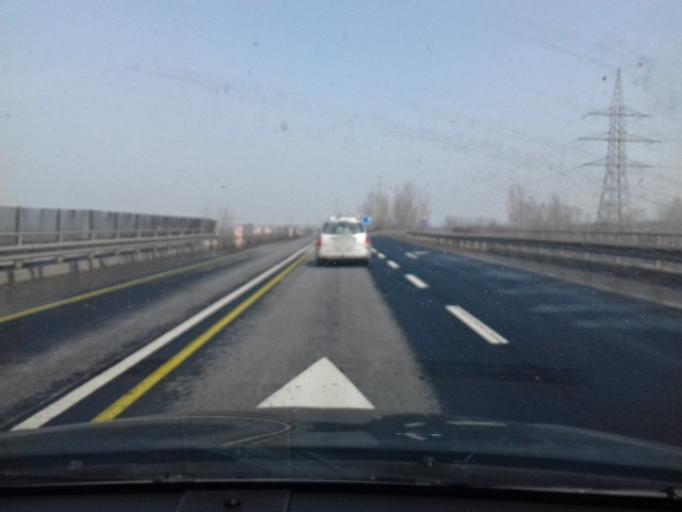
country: HU
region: Pest
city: Szod
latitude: 47.7459
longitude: 19.1762
